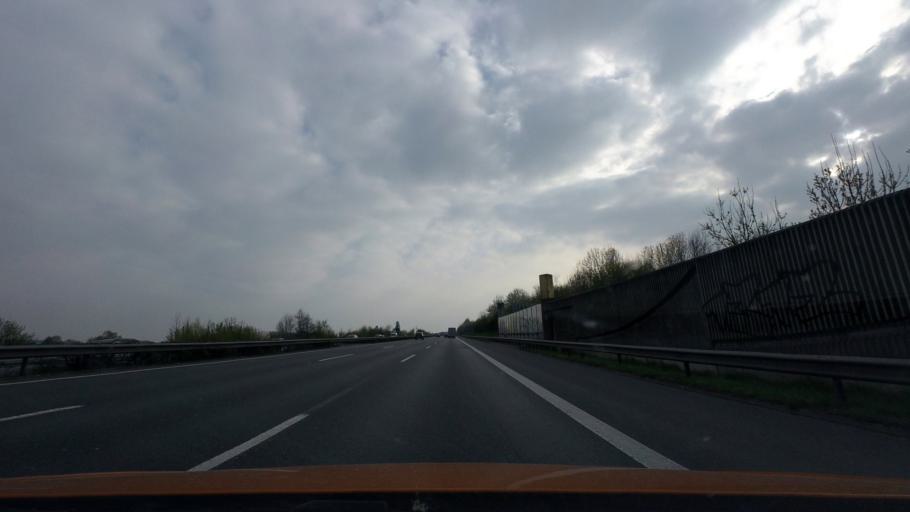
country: DE
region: North Rhine-Westphalia
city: Bad Oeynhausen
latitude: 52.1792
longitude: 8.8212
